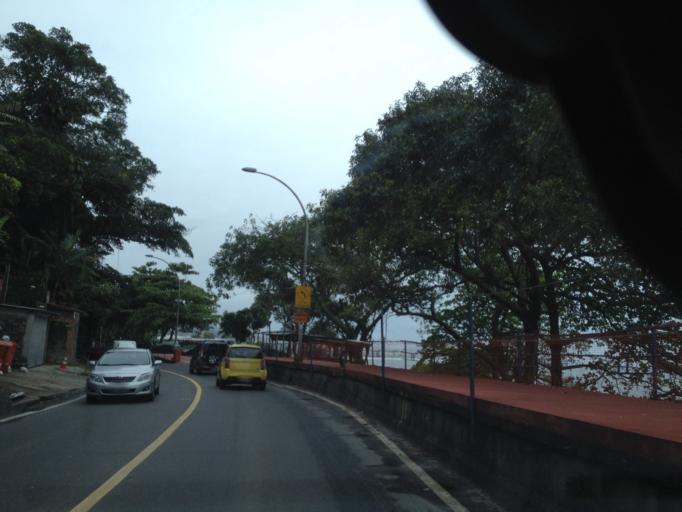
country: BR
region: Rio de Janeiro
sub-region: Rio De Janeiro
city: Rio de Janeiro
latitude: -22.9967
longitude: -43.2364
